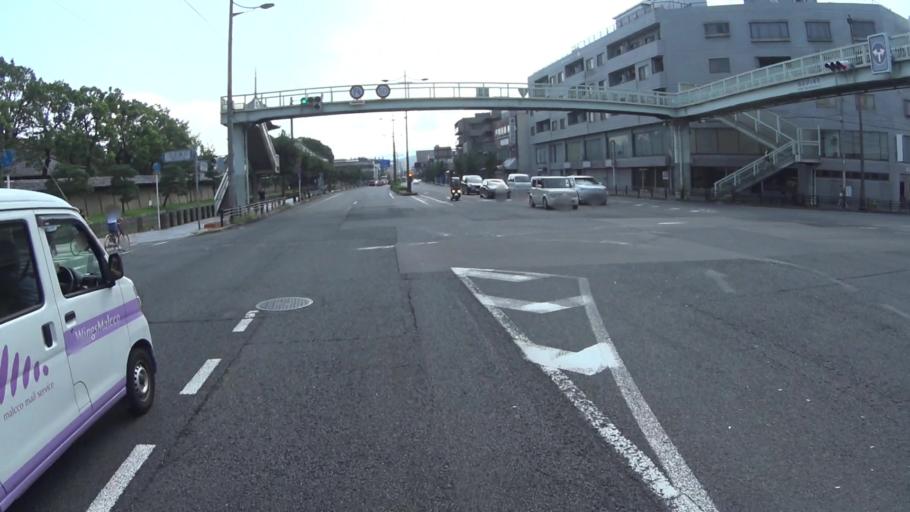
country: JP
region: Kyoto
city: Kyoto
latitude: 34.9792
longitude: 135.7536
